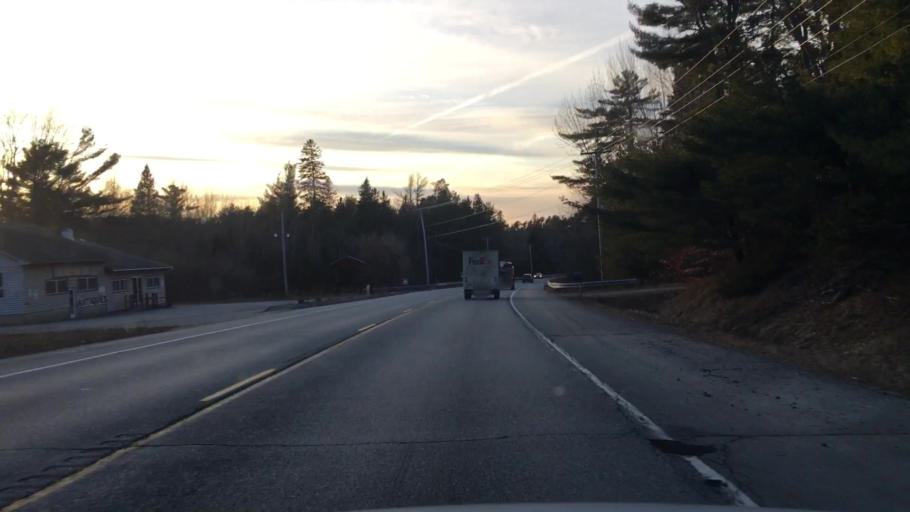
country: US
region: Maine
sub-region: Penobscot County
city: Holden
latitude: 44.7546
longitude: -68.6765
